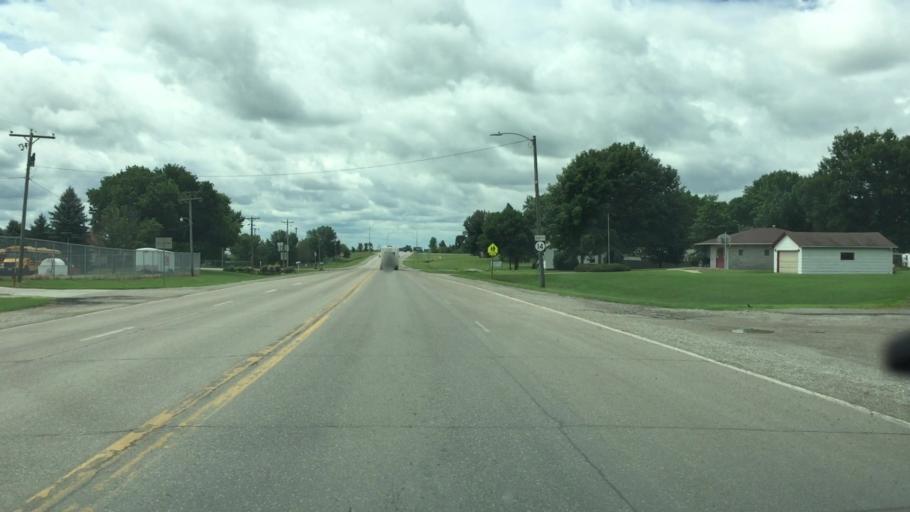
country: US
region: Iowa
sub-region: Jasper County
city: Monroe
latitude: 41.5169
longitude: -93.1017
